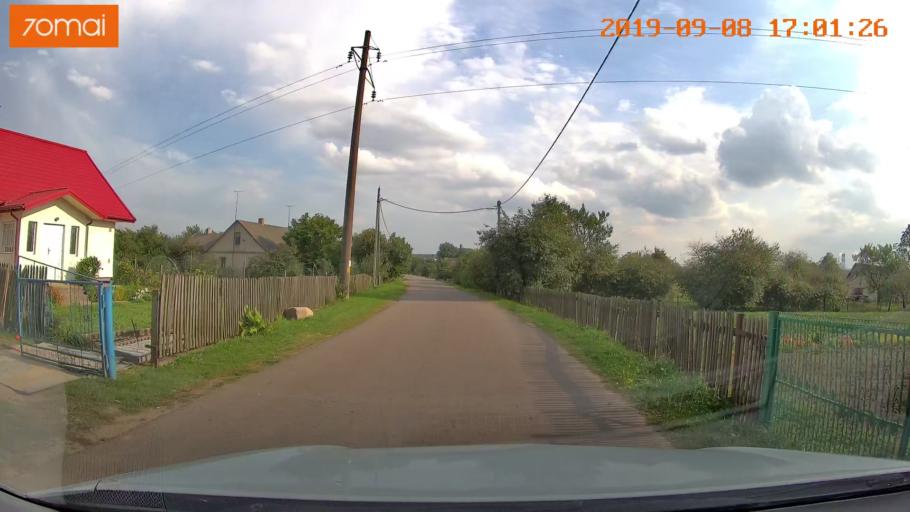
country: BY
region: Grodnenskaya
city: Hrodna
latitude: 53.7106
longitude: 23.9345
